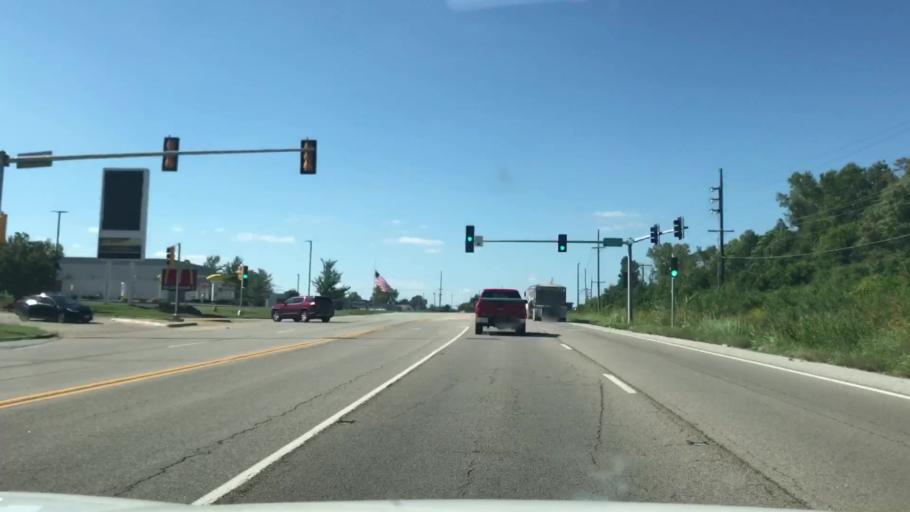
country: US
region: Illinois
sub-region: Saint Clair County
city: Swansea
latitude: 38.5445
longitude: -90.0505
